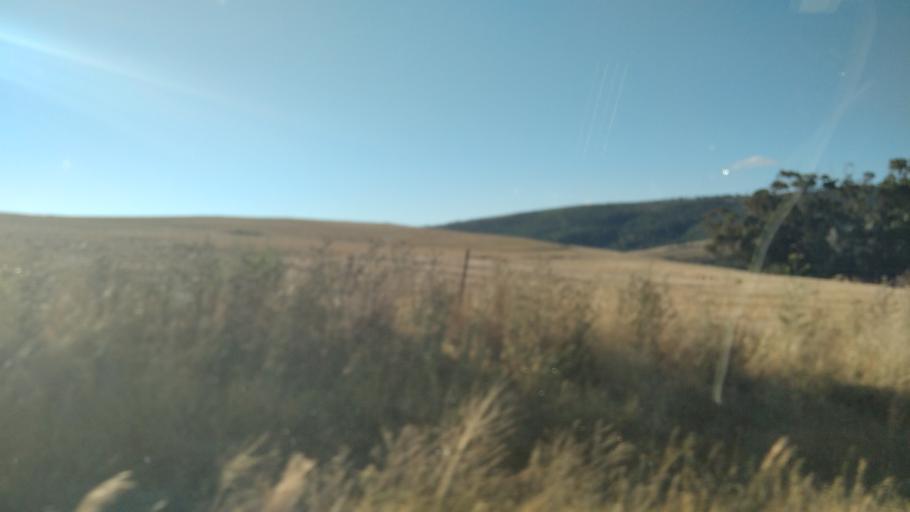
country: ZA
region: Western Cape
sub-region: Overberg District Municipality
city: Caledon
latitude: -34.1249
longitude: 19.2979
